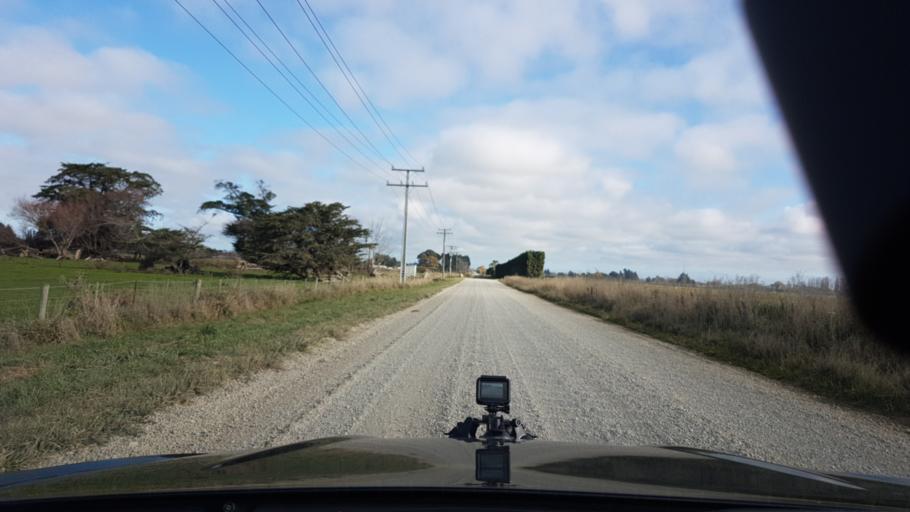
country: NZ
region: Canterbury
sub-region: Waimakariri District
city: Woodend
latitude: -43.3222
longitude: 172.6252
